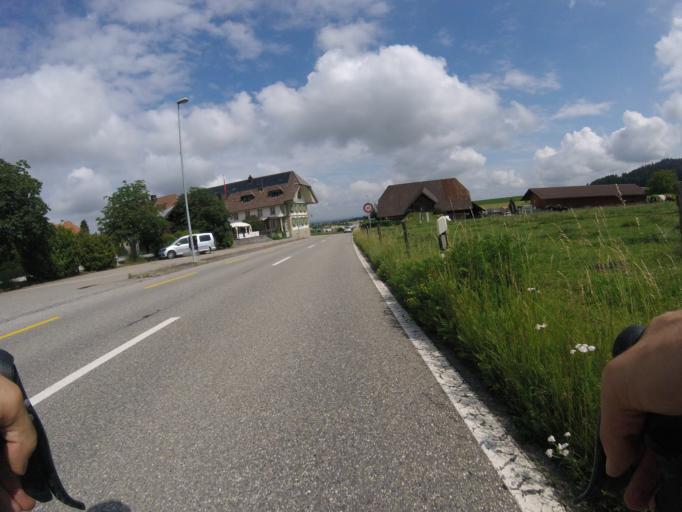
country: CH
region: Bern
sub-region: Emmental District
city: Hindelbank
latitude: 47.0309
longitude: 7.5494
